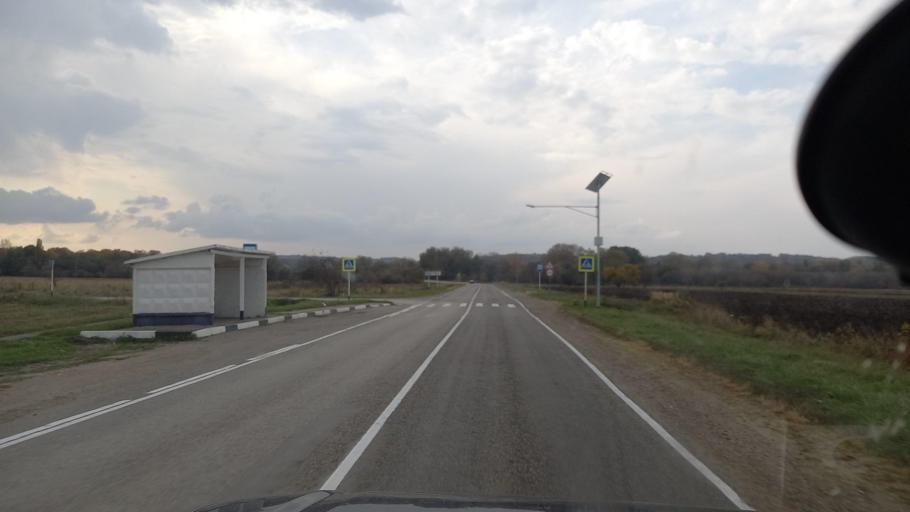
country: RU
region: Krasnodarskiy
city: Mostovskoy
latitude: 44.3922
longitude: 40.7545
